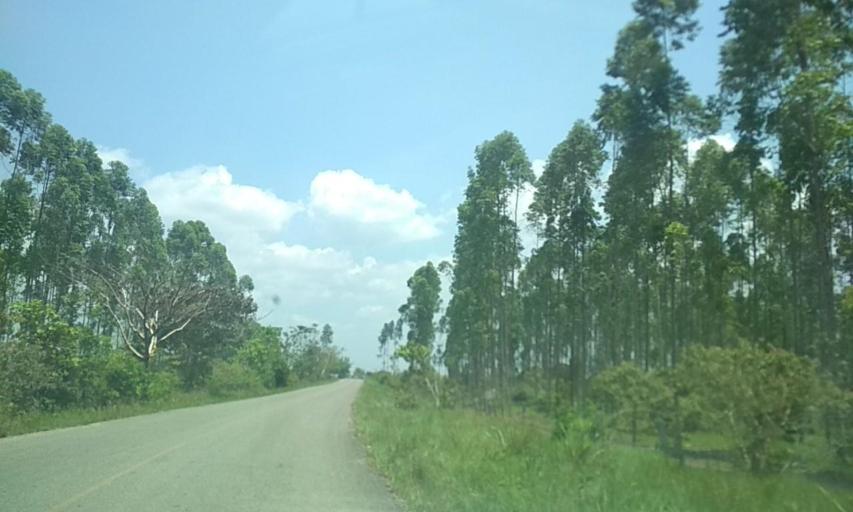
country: MX
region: Tabasco
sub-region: Huimanguillo
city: Francisco Rueda
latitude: 17.8324
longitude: -93.8751
